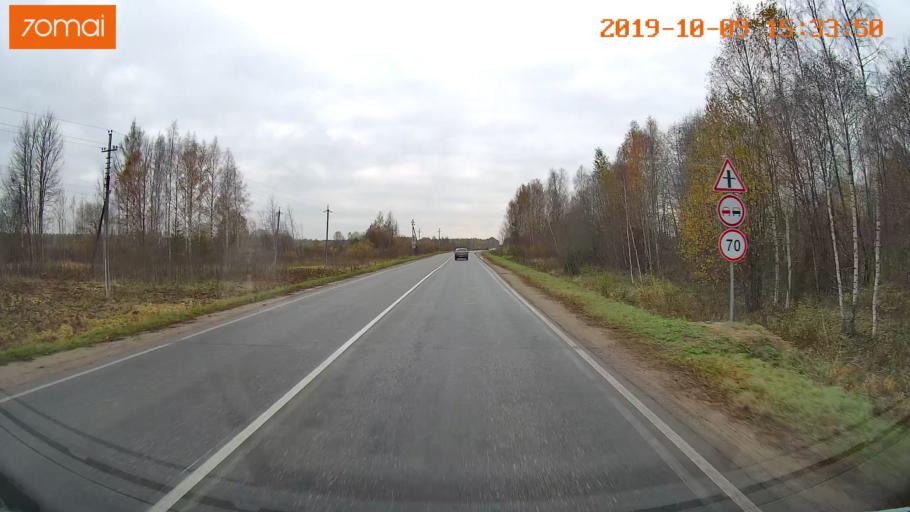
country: RU
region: Kostroma
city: Oktyabr'skiy
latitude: 57.9468
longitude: 41.2566
